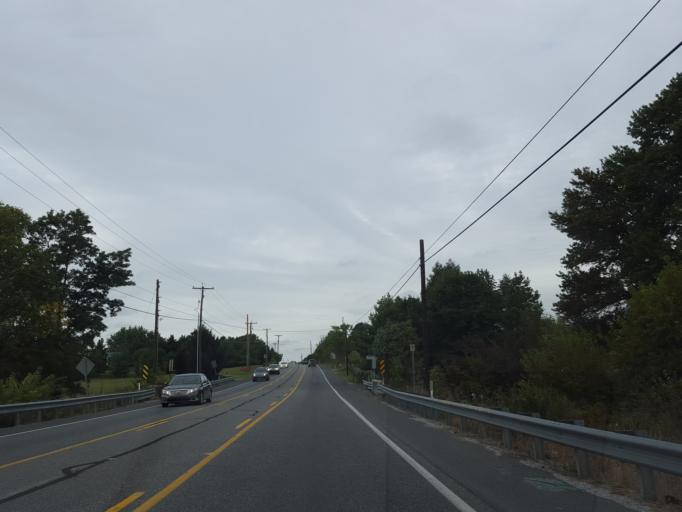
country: US
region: Pennsylvania
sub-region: York County
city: Spring Grove
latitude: 39.9202
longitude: -76.9010
